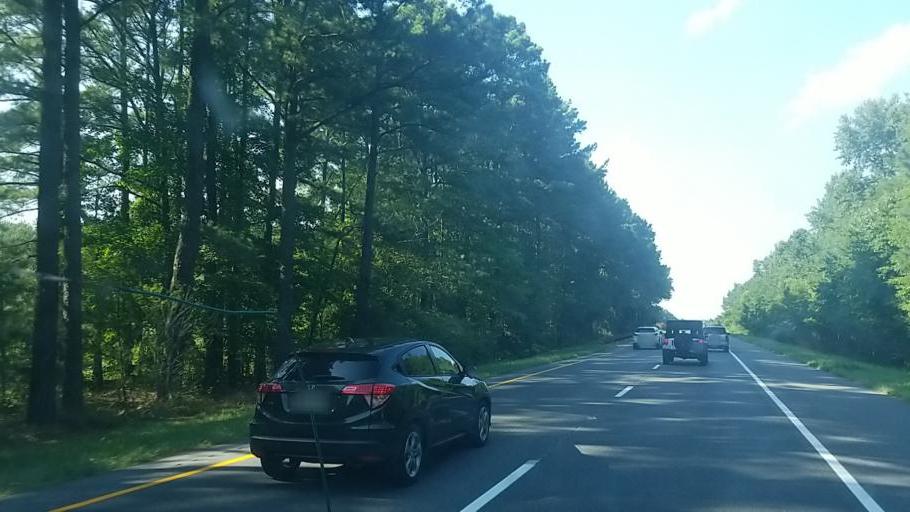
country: US
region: Maryland
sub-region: Worcester County
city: Berlin
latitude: 38.3517
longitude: -75.2143
